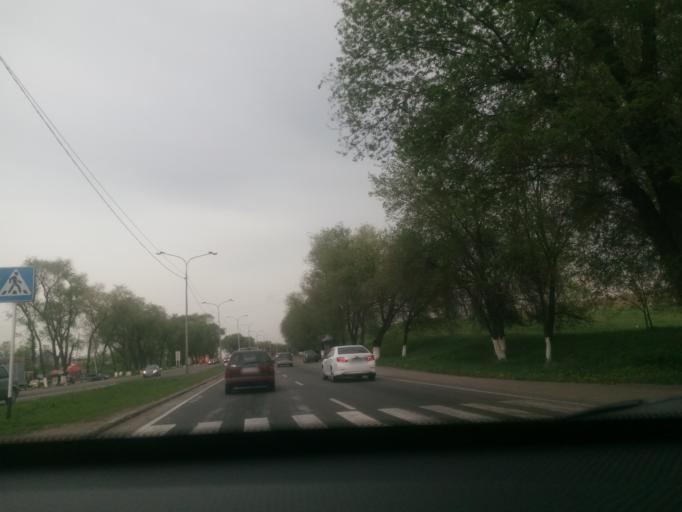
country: KZ
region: Almaty Oblysy
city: Burunday
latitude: 43.2235
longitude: 76.7219
